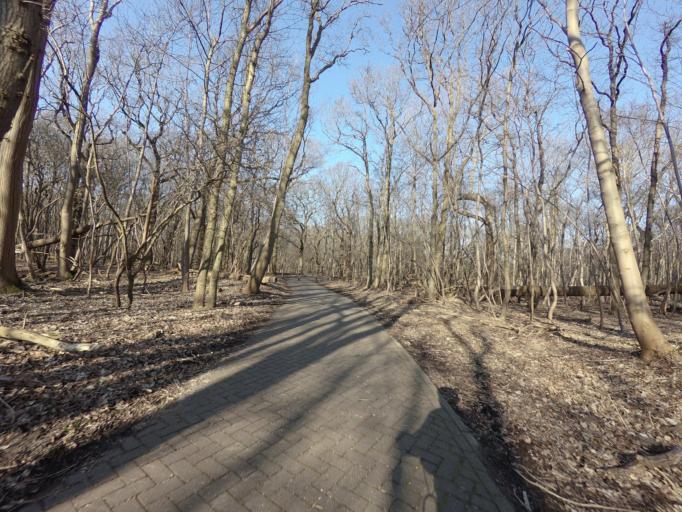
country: NL
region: North Holland
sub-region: Gemeente Velsen
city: Velsen-Zuid
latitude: 52.4491
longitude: 4.6121
